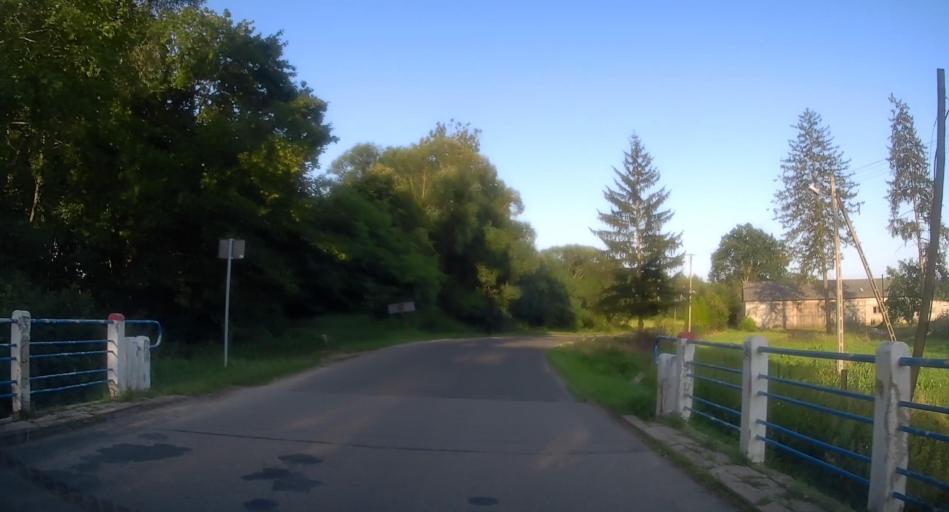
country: PL
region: Lodz Voivodeship
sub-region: Powiat skierniewicki
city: Kaweczyn Nowy
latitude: 51.9001
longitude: 20.3007
